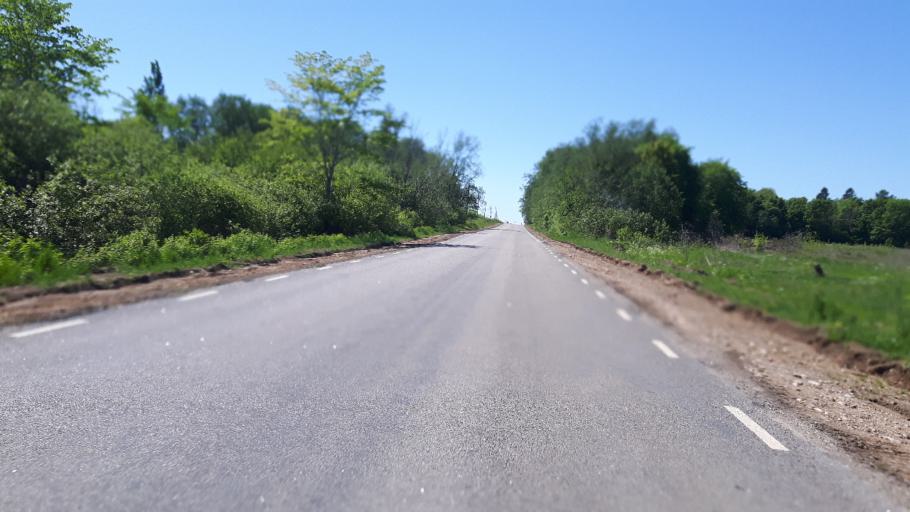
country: EE
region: Ida-Virumaa
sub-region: Narva-Joesuu linn
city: Narva-Joesuu
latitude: 59.4067
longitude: 27.9417
